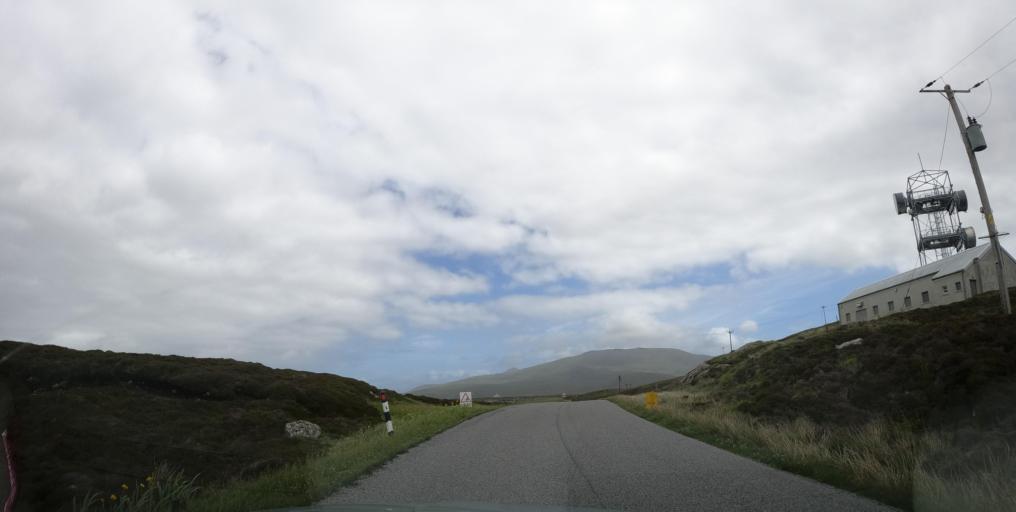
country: GB
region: Scotland
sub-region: Eilean Siar
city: Isle of South Uist
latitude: 57.2349
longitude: -7.3964
